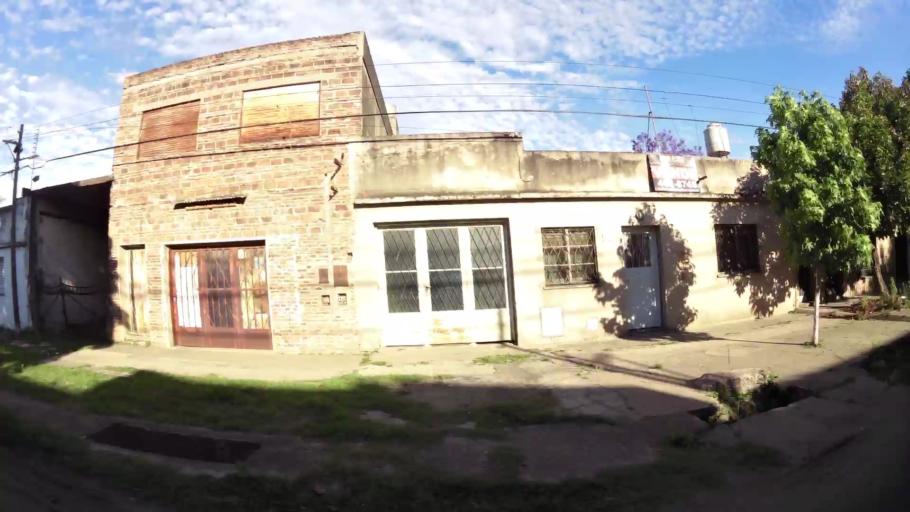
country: AR
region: Santa Fe
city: Gobernador Galvez
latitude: -32.9888
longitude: -60.6689
